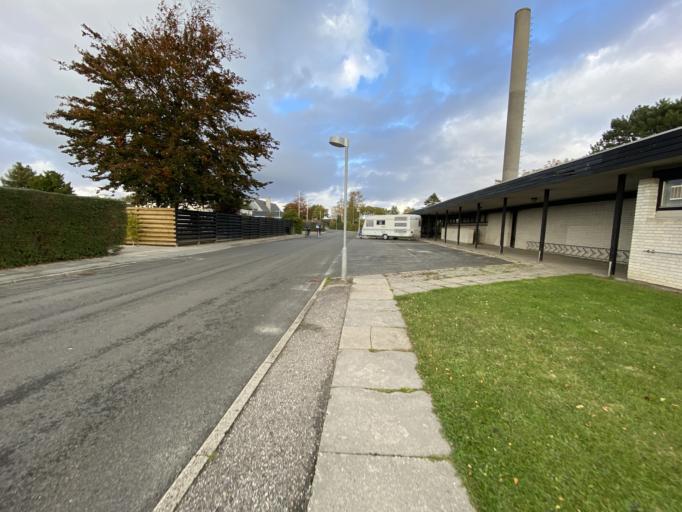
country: DK
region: Capital Region
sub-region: Dragor Kommune
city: Dragor
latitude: 55.5891
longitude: 12.6370
